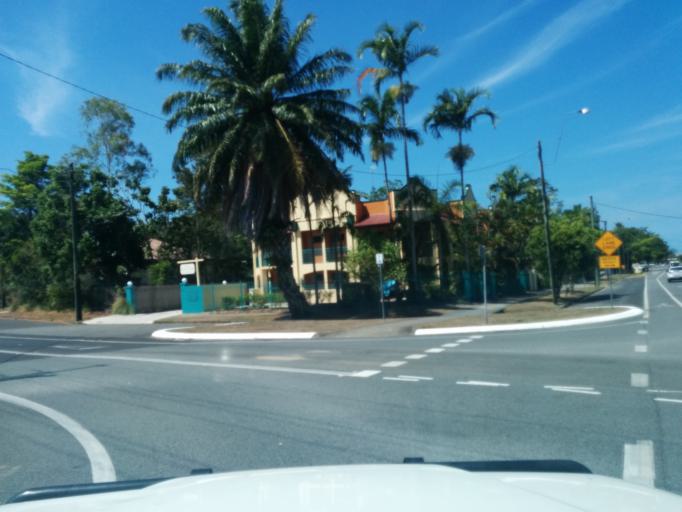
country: AU
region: Queensland
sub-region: Cairns
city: Cairns
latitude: -16.9115
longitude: 145.7563
